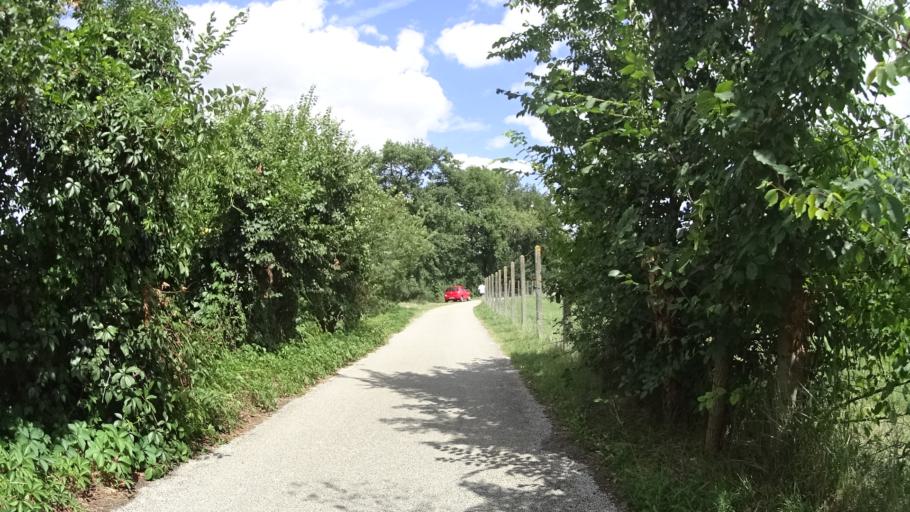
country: FR
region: Centre
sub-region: Departement d'Indre-et-Loire
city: Saint-Pierre-des-Corps
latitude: 47.4002
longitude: 0.7353
